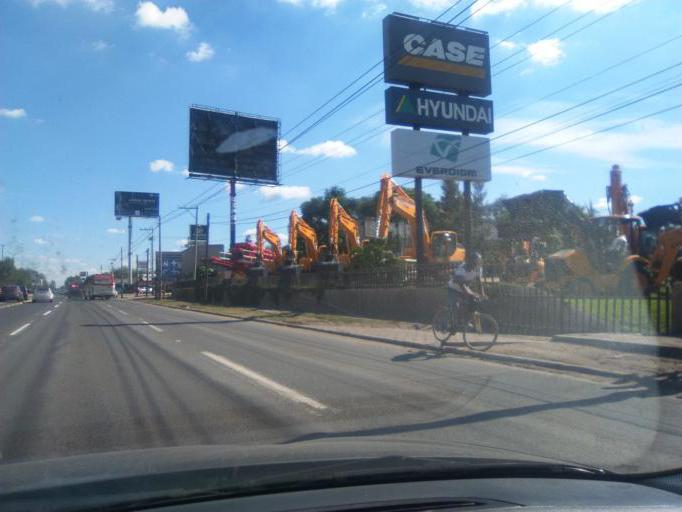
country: MX
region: Guanajuato
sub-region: Leon
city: Fraccionamiento Paraiso Real
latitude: 21.0815
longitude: -101.6100
